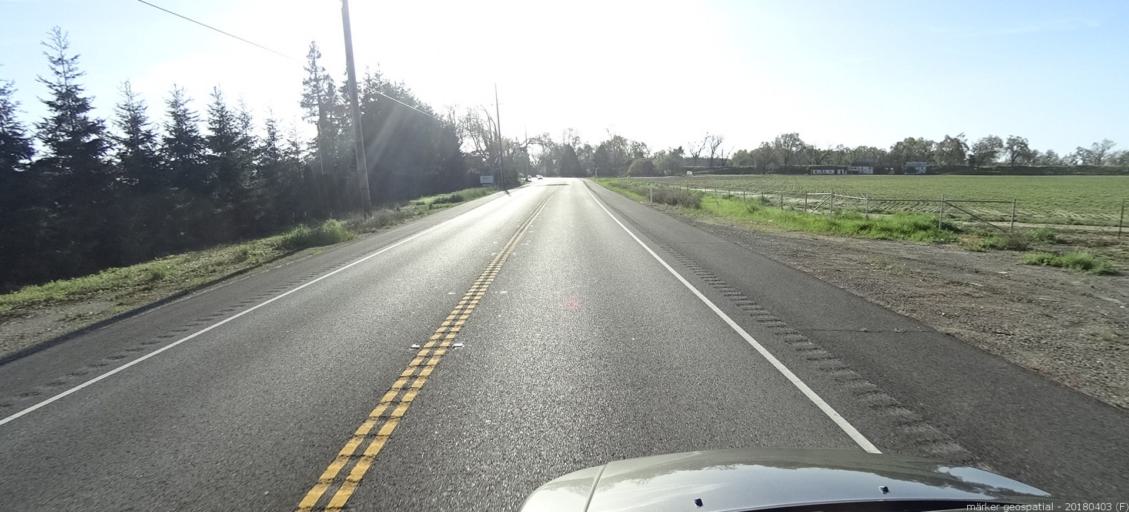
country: US
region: California
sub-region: Sacramento County
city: Rancho Murieta
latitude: 38.4933
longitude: -121.1778
